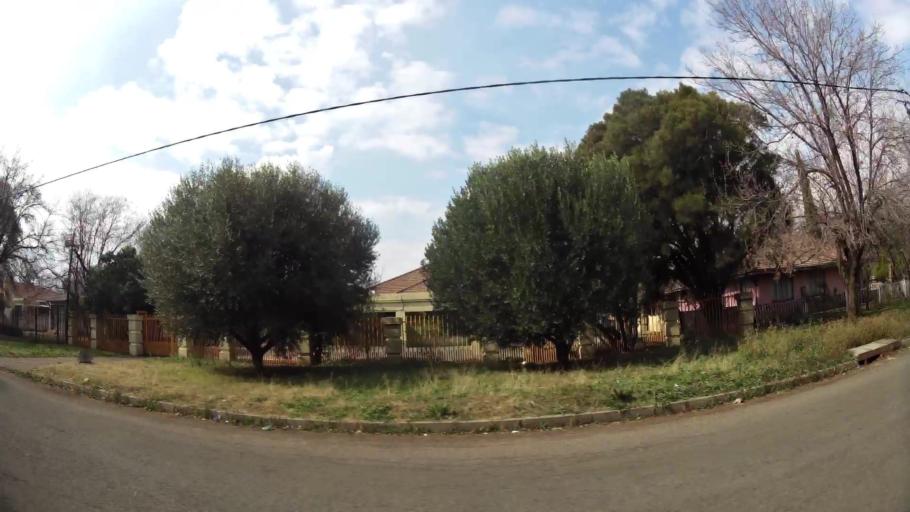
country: ZA
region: Gauteng
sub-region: Sedibeng District Municipality
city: Vereeniging
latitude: -26.6806
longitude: 27.9193
